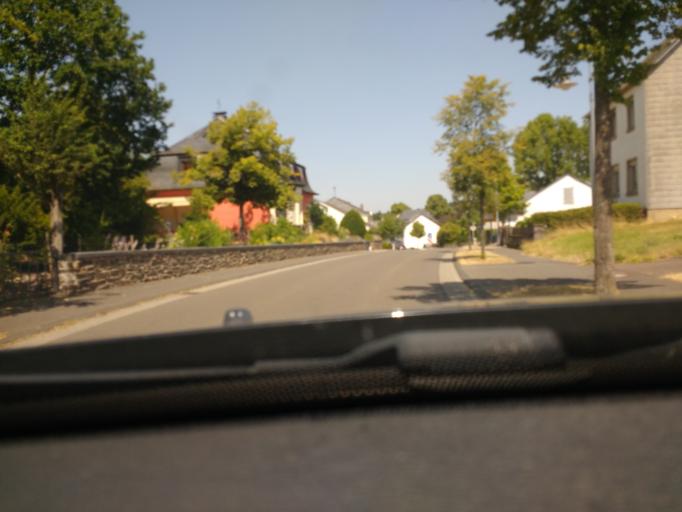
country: DE
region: Rheinland-Pfalz
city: Manderscheid
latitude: 50.0907
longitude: 6.8074
